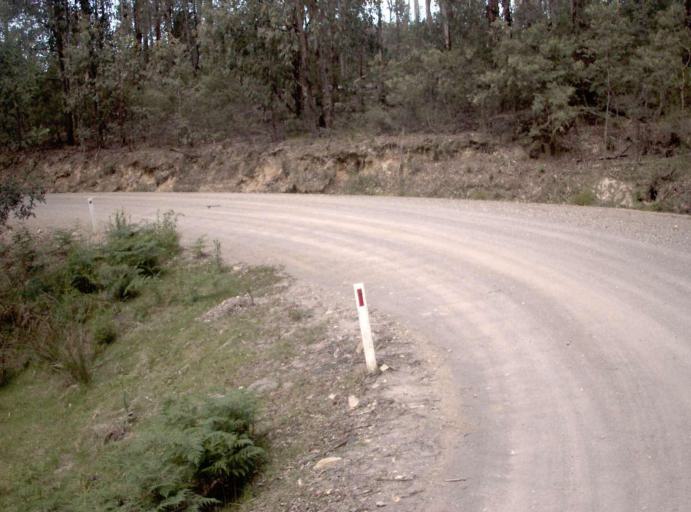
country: AU
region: New South Wales
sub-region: Bombala
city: Bombala
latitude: -37.1882
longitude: 148.7048
